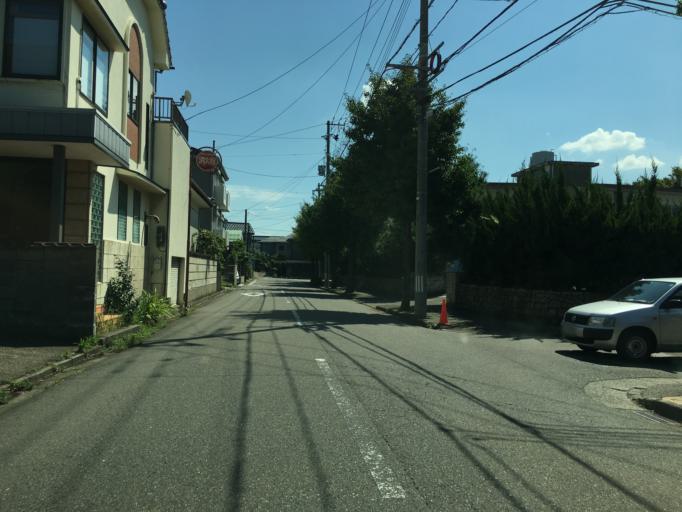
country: JP
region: Niigata
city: Niigata-shi
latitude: 37.9175
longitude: 139.0266
